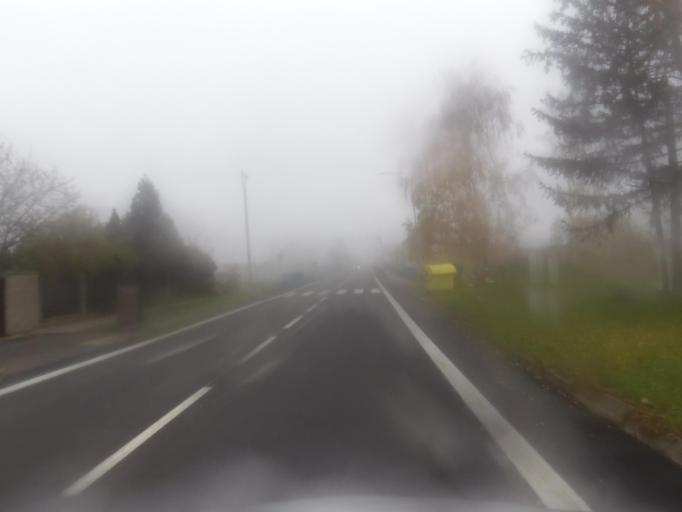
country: CZ
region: Ustecky
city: Peruc
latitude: 50.4022
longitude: 13.9484
